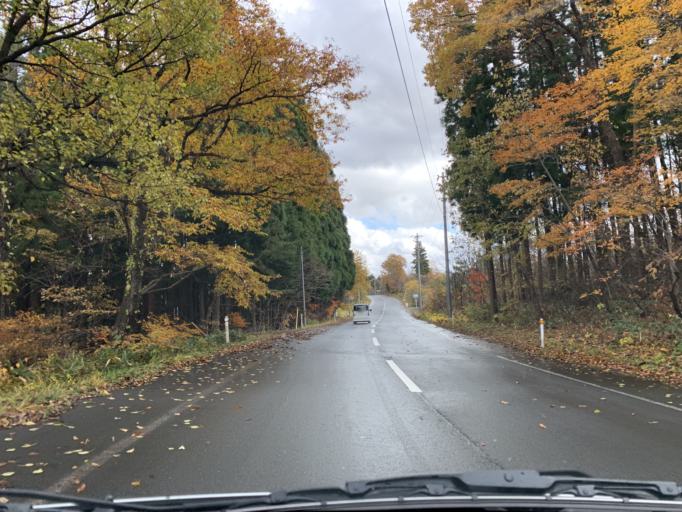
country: JP
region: Iwate
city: Mizusawa
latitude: 39.1134
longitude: 140.9582
